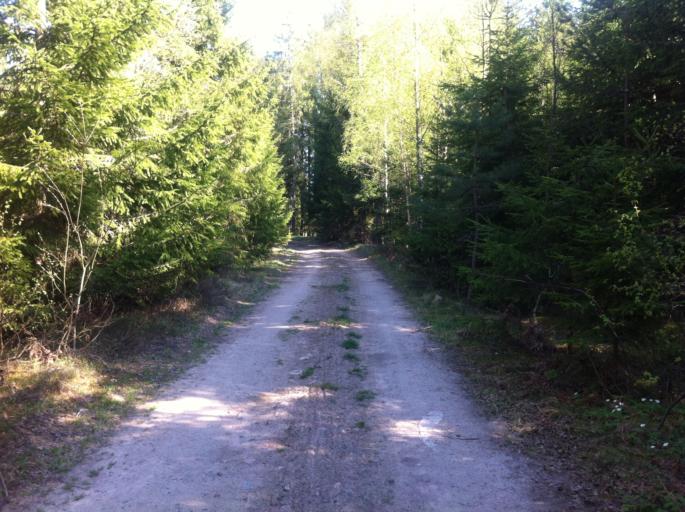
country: SE
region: Joenkoeping
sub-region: Mullsjo Kommun
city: Mullsjoe
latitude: 57.8803
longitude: 13.9107
